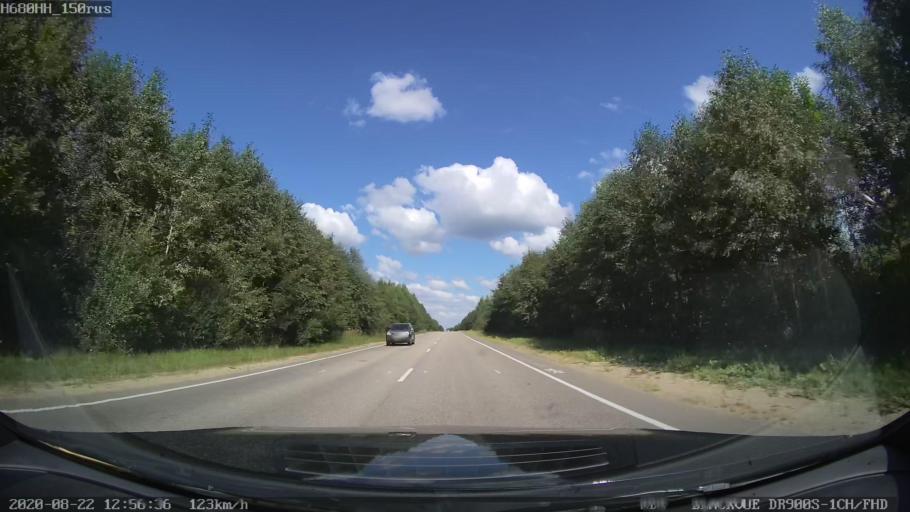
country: RU
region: Tverskaya
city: Rameshki
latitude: 57.5591
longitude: 36.3190
